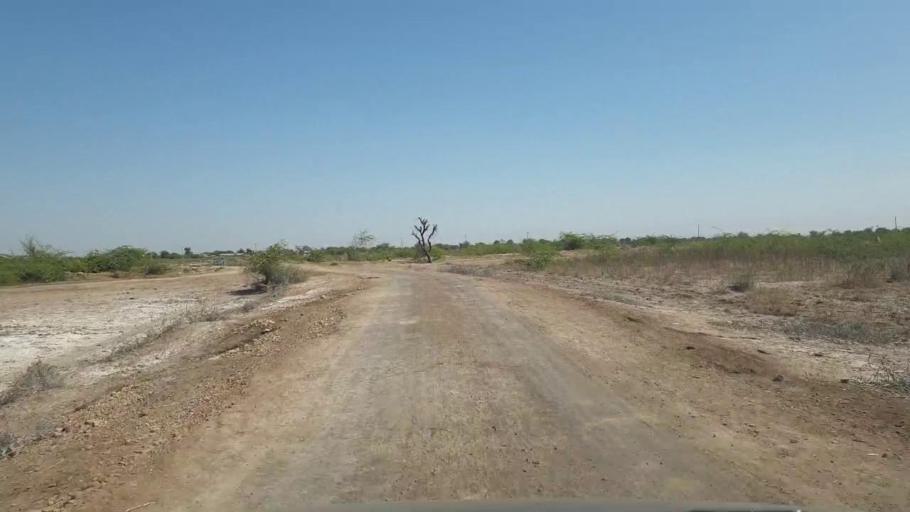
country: PK
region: Sindh
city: Dhoro Naro
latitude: 25.4078
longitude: 69.6158
